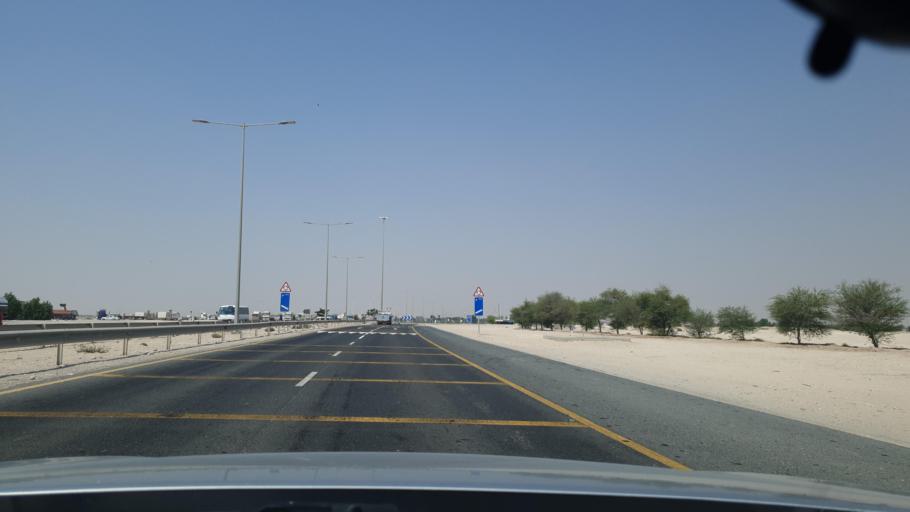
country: QA
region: Al Khawr
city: Al Khawr
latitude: 25.7200
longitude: 51.5011
